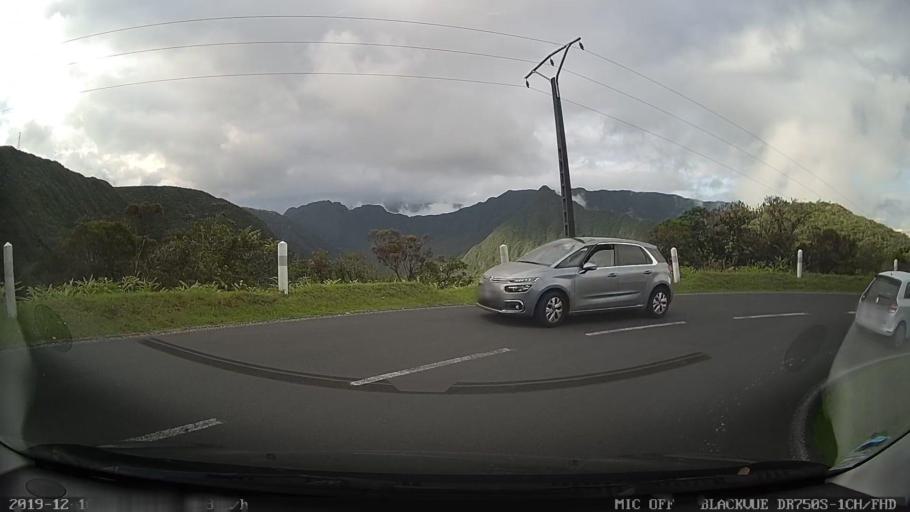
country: RE
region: Reunion
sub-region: Reunion
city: Cilaos
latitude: -21.1589
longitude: 55.5955
